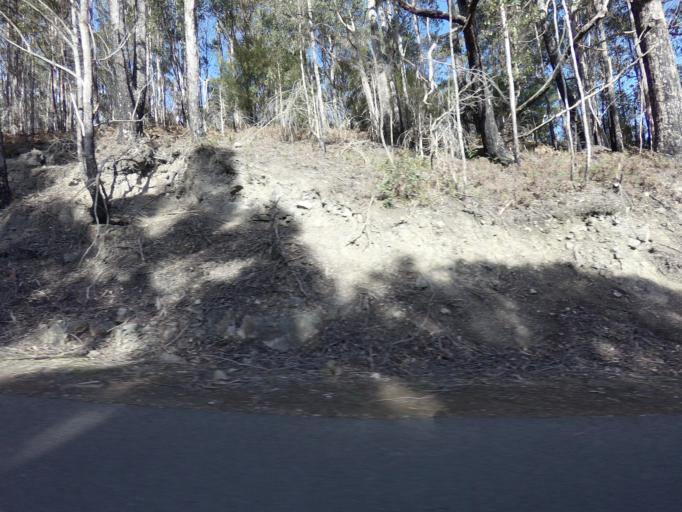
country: AU
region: Tasmania
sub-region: Huon Valley
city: Cygnet
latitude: -43.1744
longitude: 147.1584
